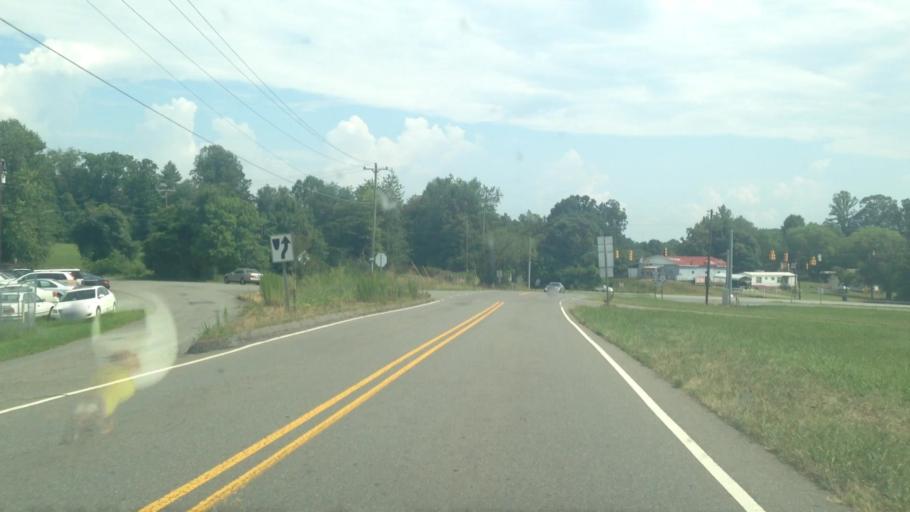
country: US
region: North Carolina
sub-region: Surry County
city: Flat Rock
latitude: 36.4716
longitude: -80.5736
